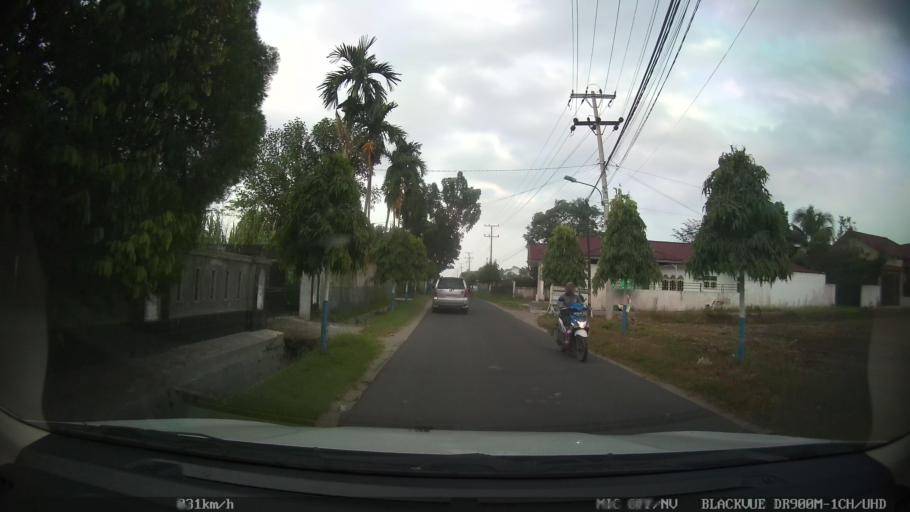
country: ID
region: North Sumatra
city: Sunggal
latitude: 3.5596
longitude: 98.5585
